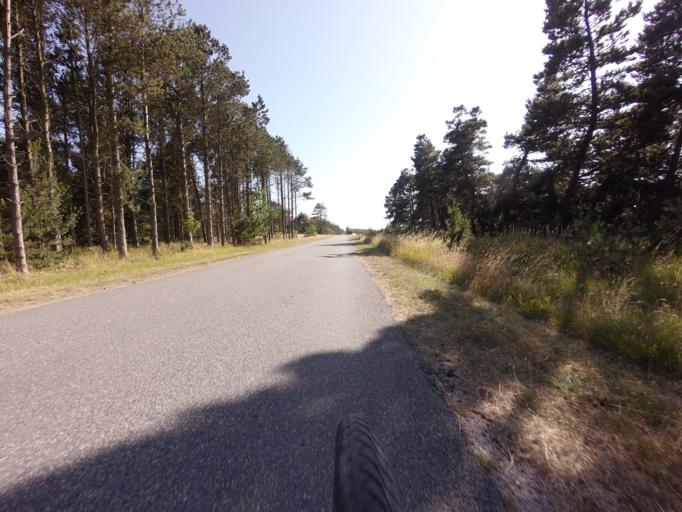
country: DK
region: North Denmark
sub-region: Laeso Kommune
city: Byrum
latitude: 57.2776
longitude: 10.9095
